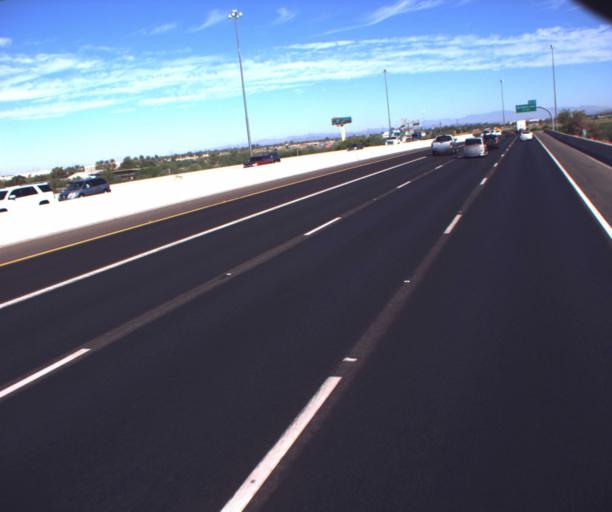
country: US
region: Arizona
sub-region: Maricopa County
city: Peoria
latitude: 33.5369
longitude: -112.2695
